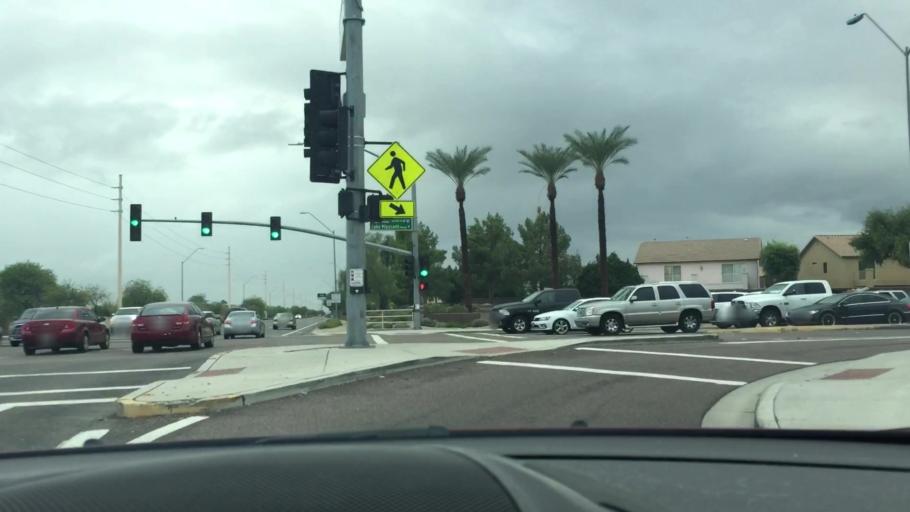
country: US
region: Arizona
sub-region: Maricopa County
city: Sun City
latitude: 33.6673
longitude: -112.2375
